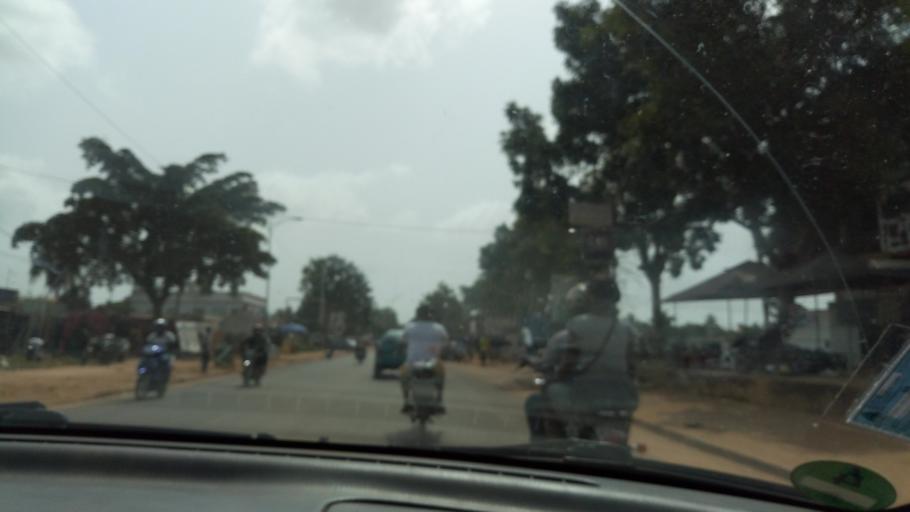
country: TG
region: Maritime
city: Lome
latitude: 6.1785
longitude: 1.1756
